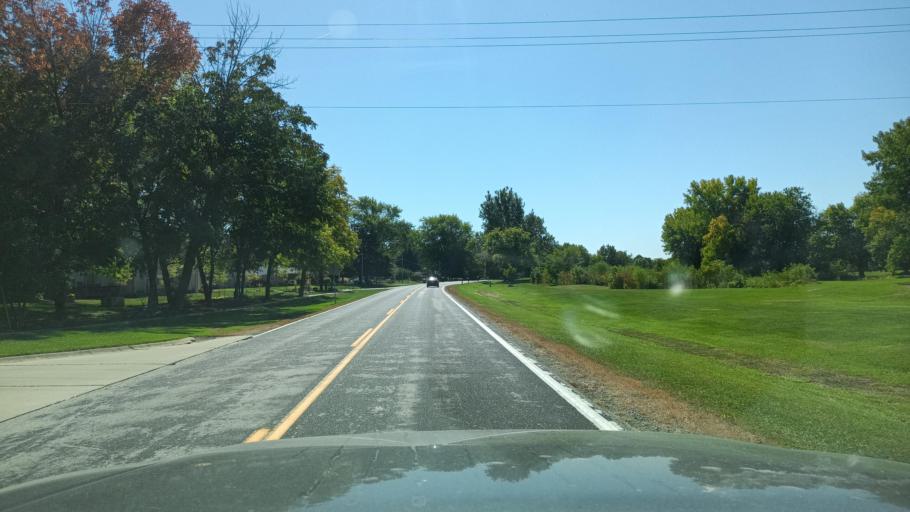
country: US
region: Illinois
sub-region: Champaign County
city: Lake of the Woods
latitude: 40.2046
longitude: -88.3709
